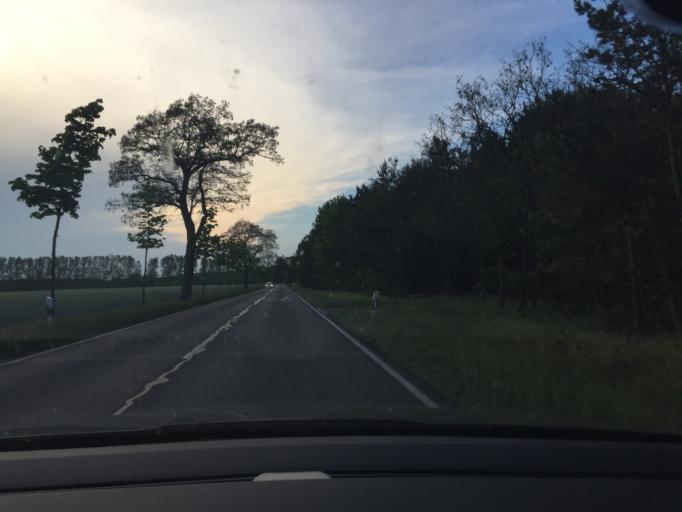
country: DE
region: Brandenburg
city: Beelitz
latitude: 52.1261
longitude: 13.0127
